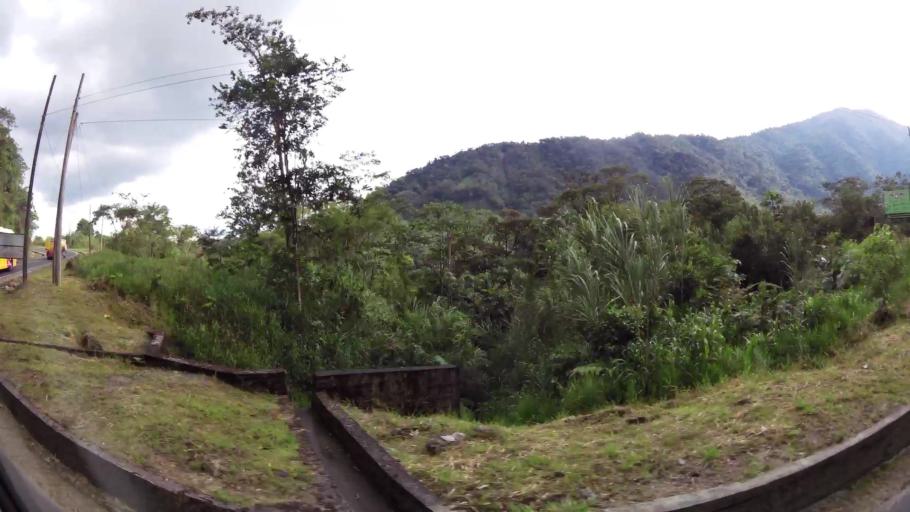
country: EC
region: Pastaza
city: Puyo
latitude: -1.4495
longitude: -78.1485
